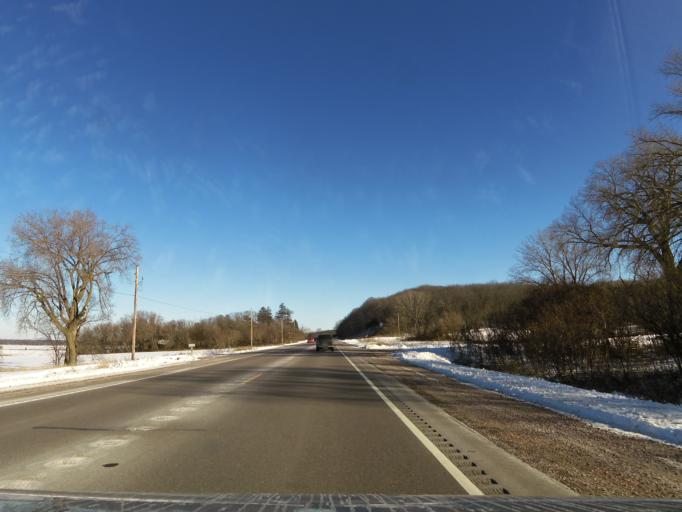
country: US
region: Wisconsin
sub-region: Columbia County
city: Portage
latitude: 43.5080
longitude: -89.5898
